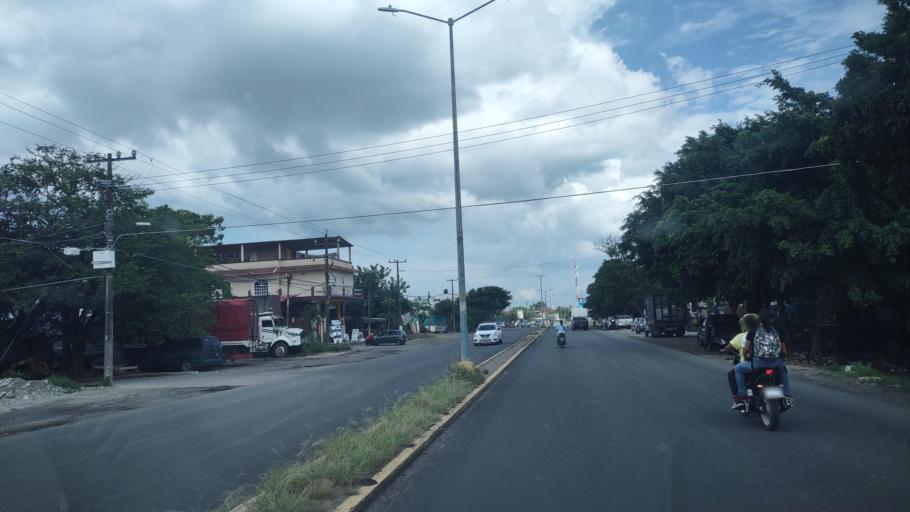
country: MX
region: Veracruz
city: Martinez de la Torre
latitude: 20.0709
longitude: -97.0691
